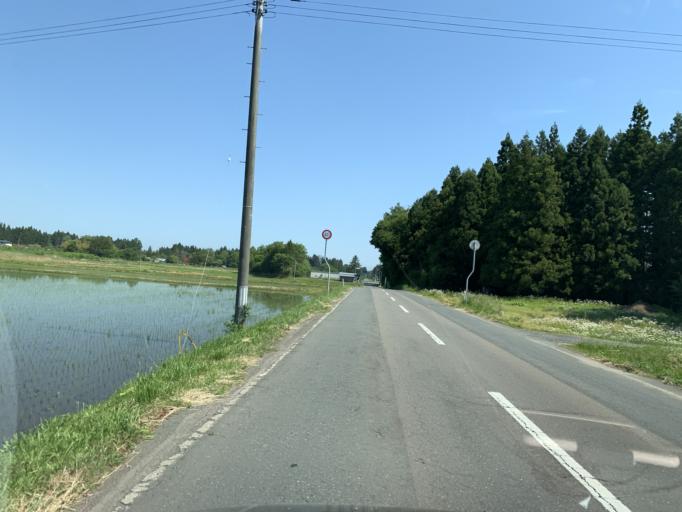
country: JP
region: Iwate
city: Mizusawa
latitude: 39.0991
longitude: 141.0757
